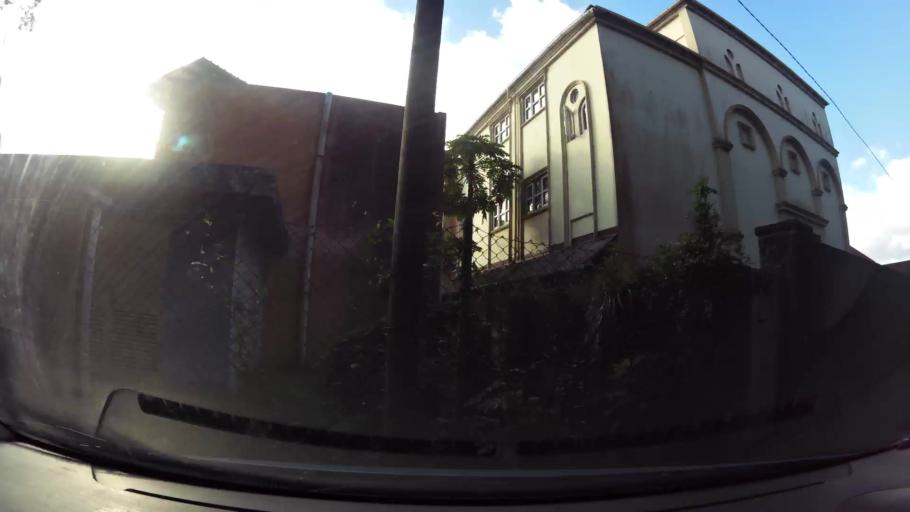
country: MU
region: Plaines Wilhems
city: Vacoas
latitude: -20.2948
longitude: 57.4950
